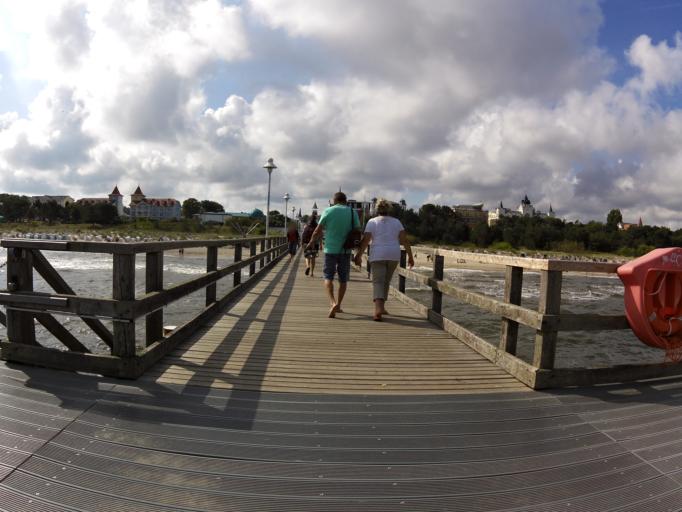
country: DE
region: Mecklenburg-Vorpommern
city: Ostseebad Zinnowitz
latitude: 54.0829
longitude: 13.9161
